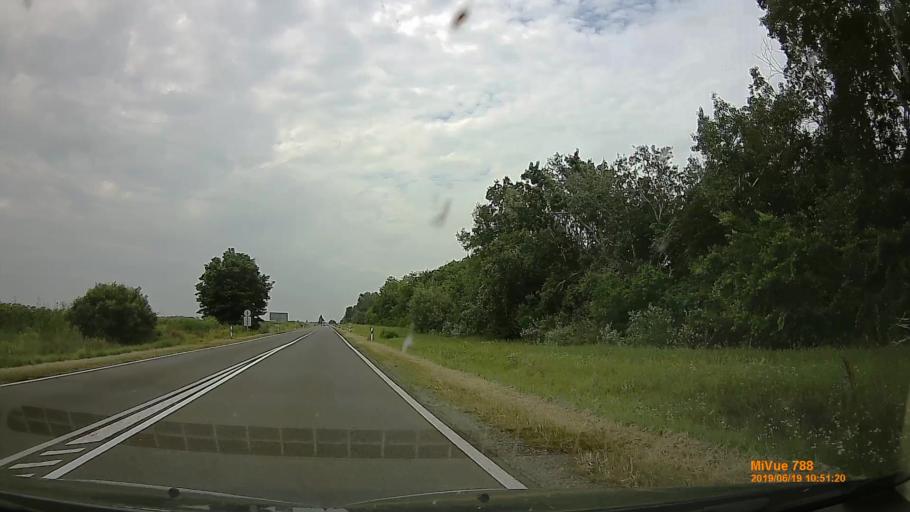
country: HU
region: Tolna
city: Dunaszentgyorgy
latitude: 46.5040
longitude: 18.7899
